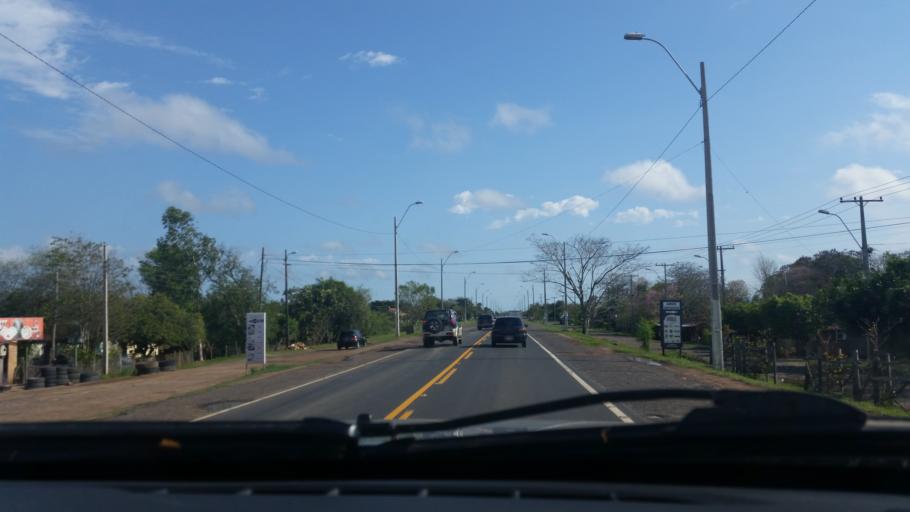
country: PY
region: Presidente Hayes
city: Benjamin Aceval
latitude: -24.9579
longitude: -57.5486
